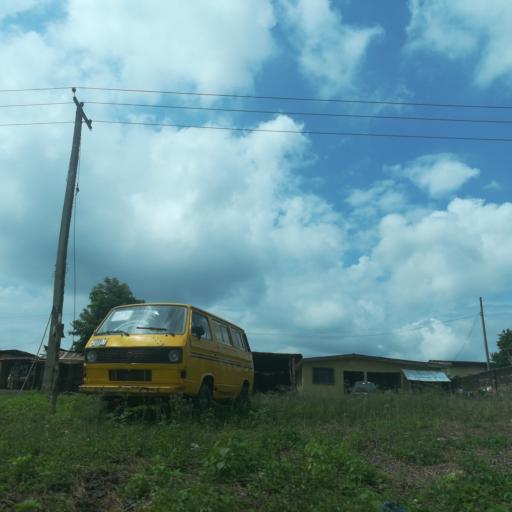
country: NG
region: Lagos
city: Ejirin
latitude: 6.6496
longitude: 3.7106
